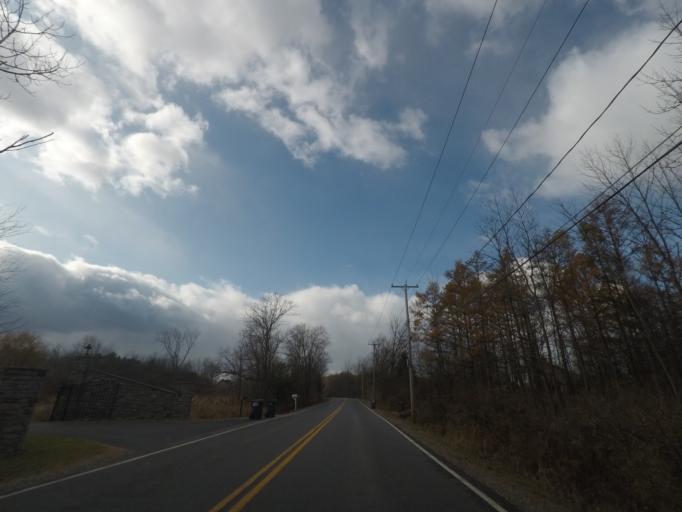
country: US
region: New York
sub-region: Saratoga County
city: Ballston Spa
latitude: 42.9633
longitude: -73.8327
